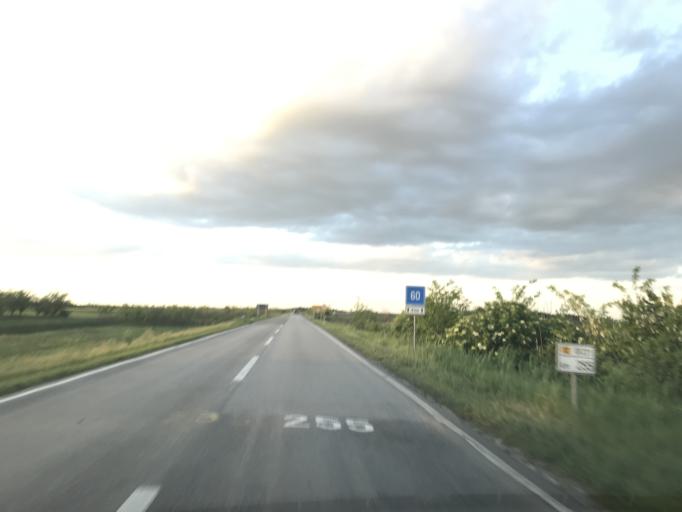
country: RS
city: Banatsko Karadordevo
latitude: 45.5972
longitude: 20.5612
